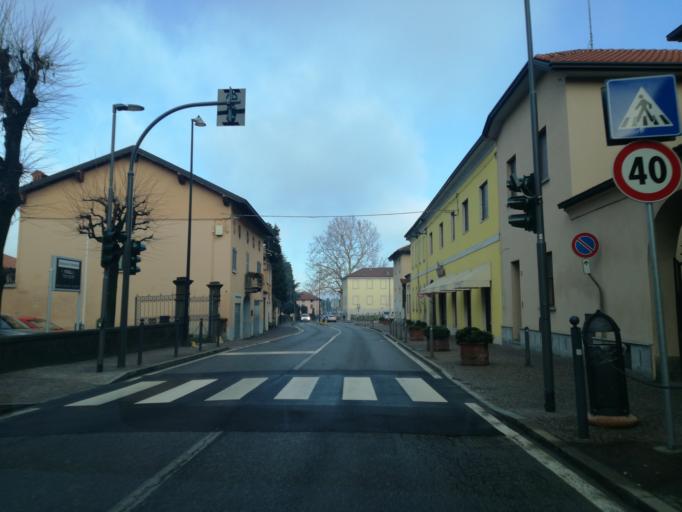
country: IT
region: Lombardy
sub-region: Provincia di Lecco
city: Verderio Superiore
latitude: 45.6687
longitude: 9.4397
